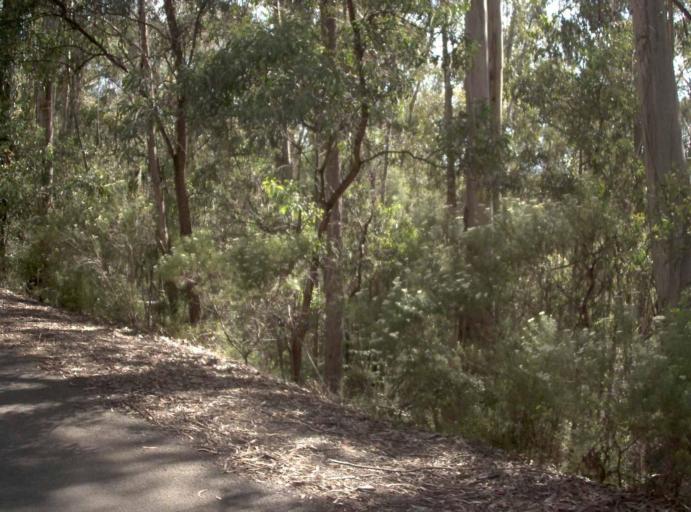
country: AU
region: Victoria
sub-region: East Gippsland
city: Lakes Entrance
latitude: -37.4214
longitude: 148.1279
